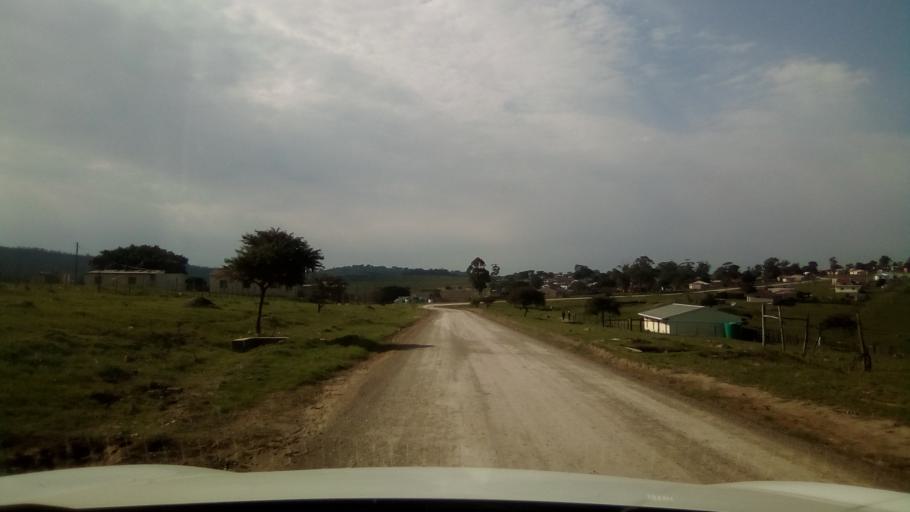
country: ZA
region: Eastern Cape
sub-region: Buffalo City Metropolitan Municipality
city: Bhisho
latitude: -32.9857
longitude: 27.2615
